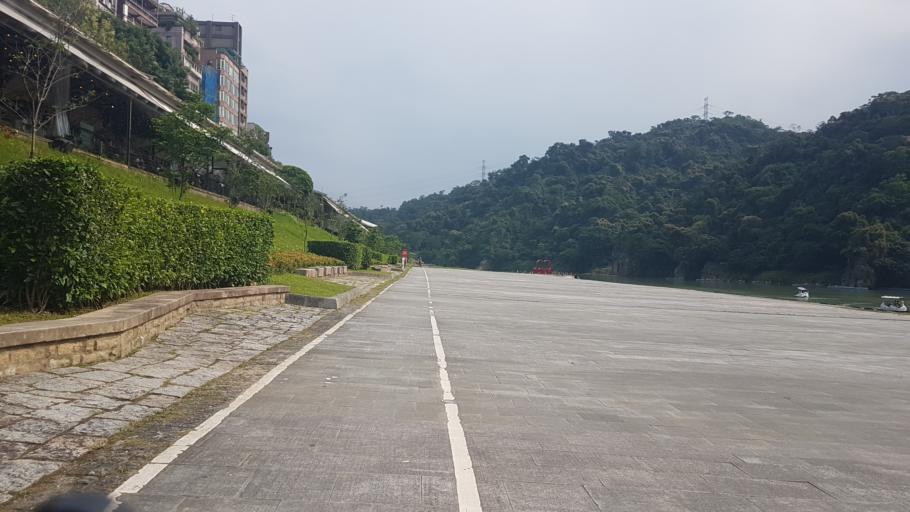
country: TW
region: Taipei
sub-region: Taipei
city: Banqiao
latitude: 24.9561
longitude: 121.5366
